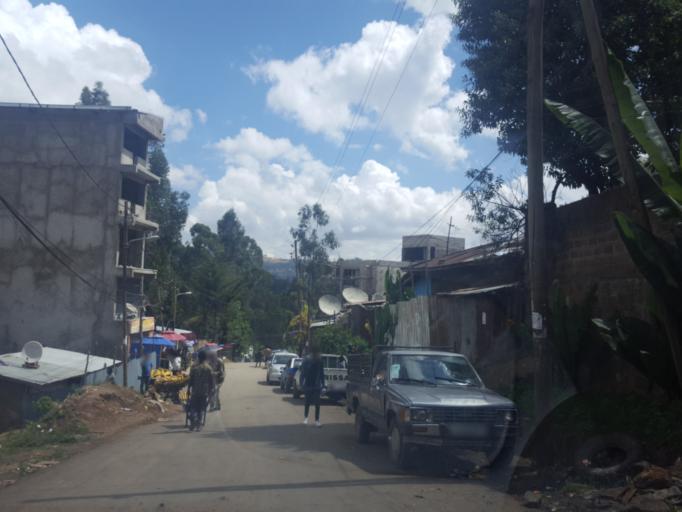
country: ET
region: Adis Abeba
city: Addis Ababa
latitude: 9.0615
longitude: 38.7627
